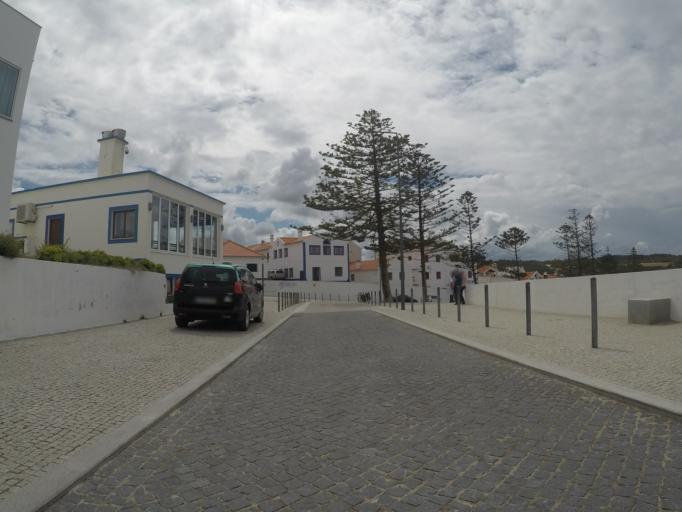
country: PT
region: Beja
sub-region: Odemira
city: Sao Teotonio
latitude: 37.5244
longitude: -8.7865
